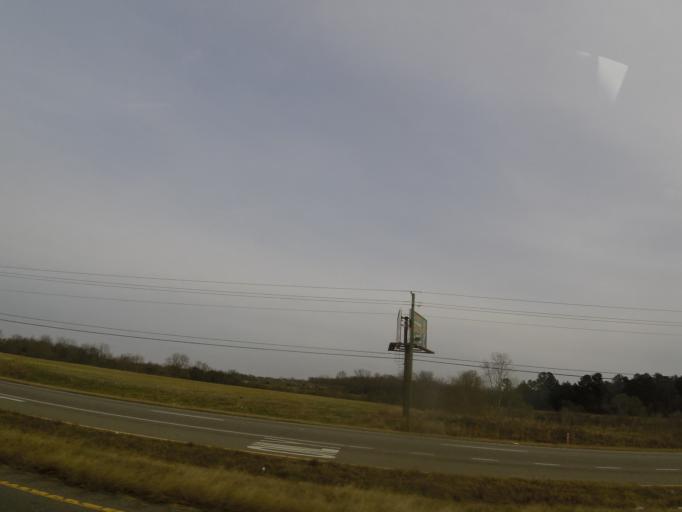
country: US
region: Alabama
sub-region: Montgomery County
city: Montgomery
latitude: 32.3053
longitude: -86.2126
